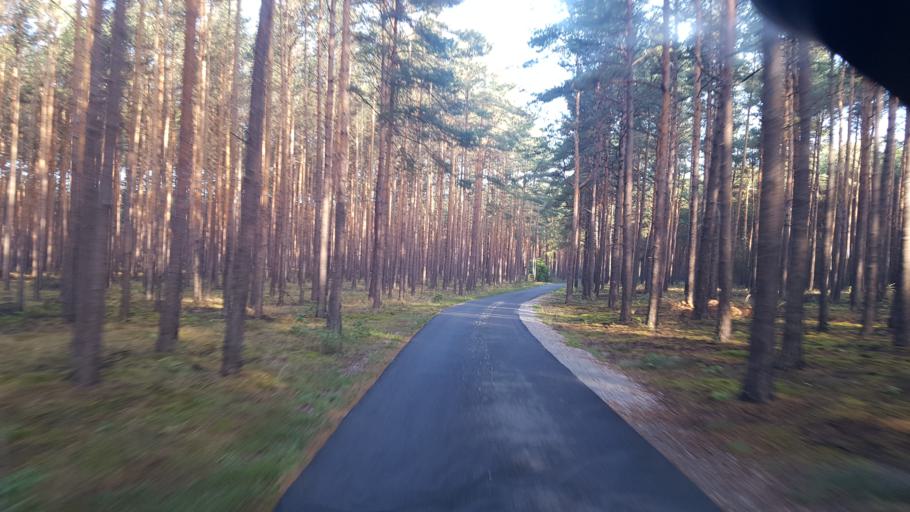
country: DE
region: Brandenburg
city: Bronkow
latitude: 51.6690
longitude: 13.8942
